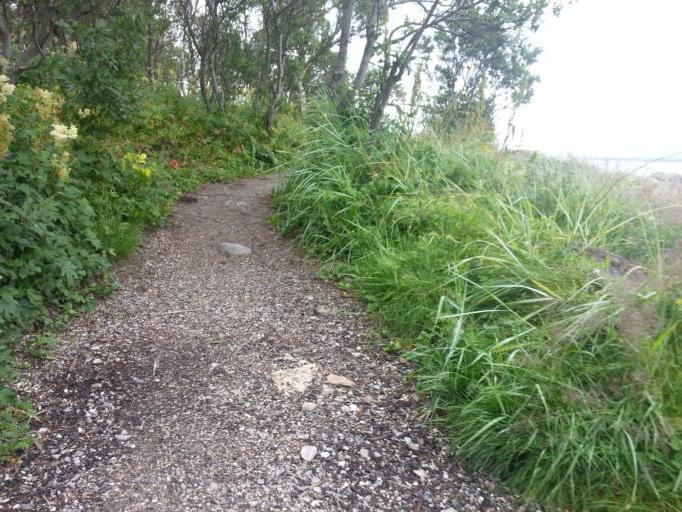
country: NO
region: Troms
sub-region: Tromso
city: Tromso
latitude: 69.6336
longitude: 18.9051
